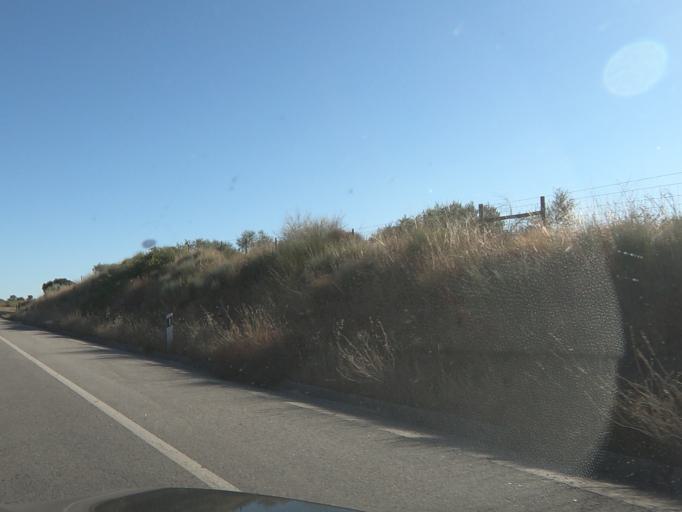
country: PT
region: Vila Real
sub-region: Valpacos
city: Valpacos
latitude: 41.5760
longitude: -7.3021
